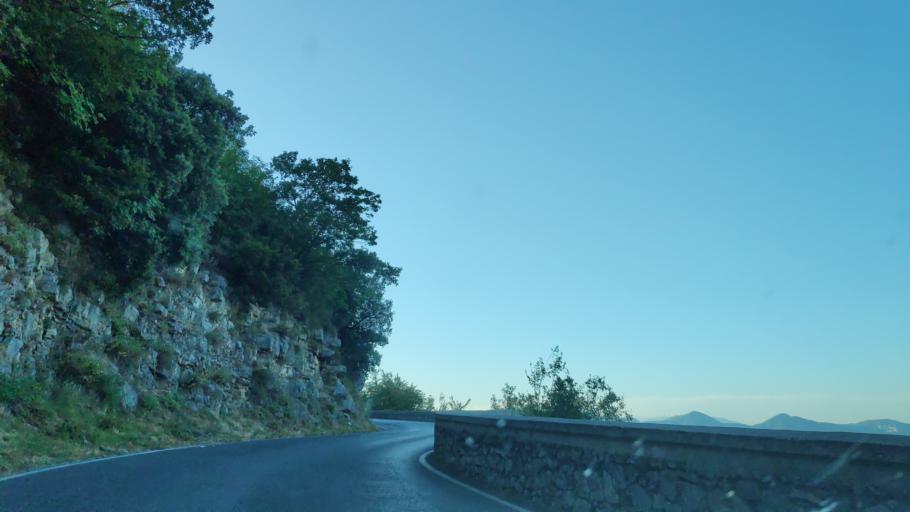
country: IT
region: Campania
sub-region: Provincia di Salerno
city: Corbara
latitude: 40.7233
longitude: 14.6060
